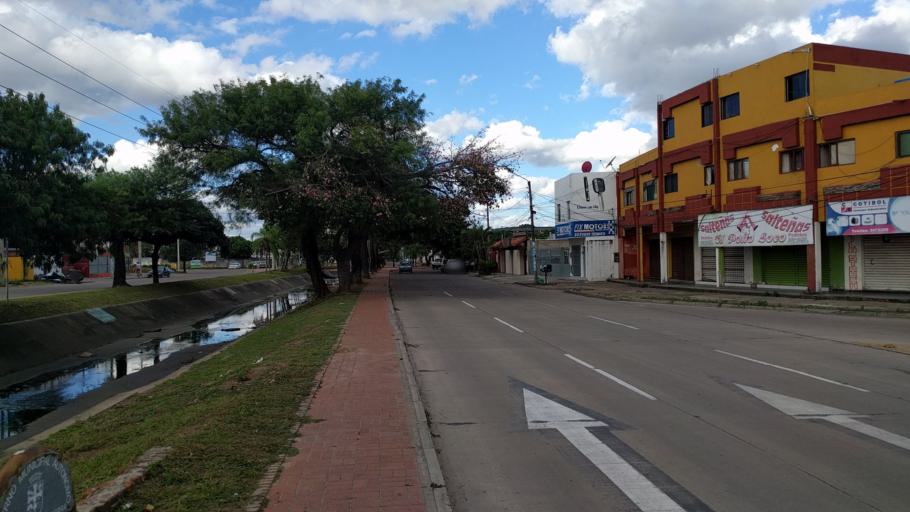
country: BO
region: Santa Cruz
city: Santa Cruz de la Sierra
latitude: -17.7766
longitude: -63.1549
